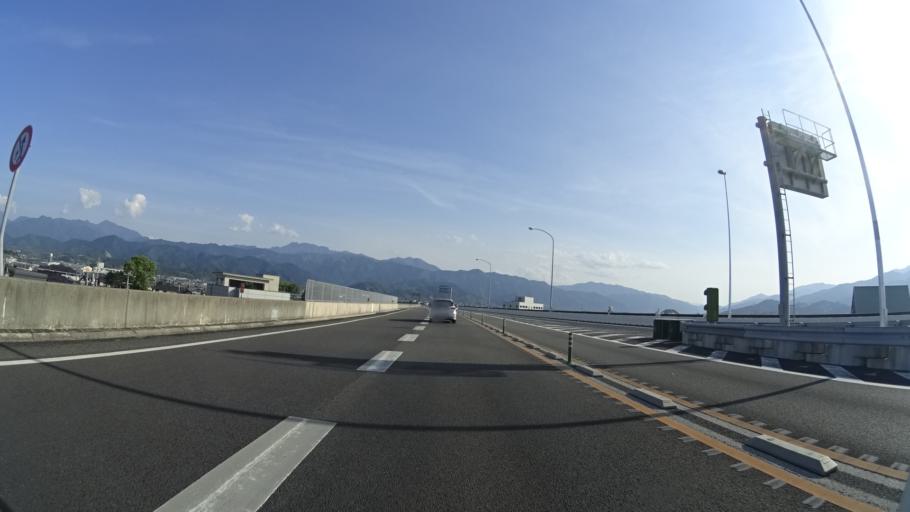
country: JP
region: Ehime
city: Saijo
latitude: 33.9157
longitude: 133.0730
